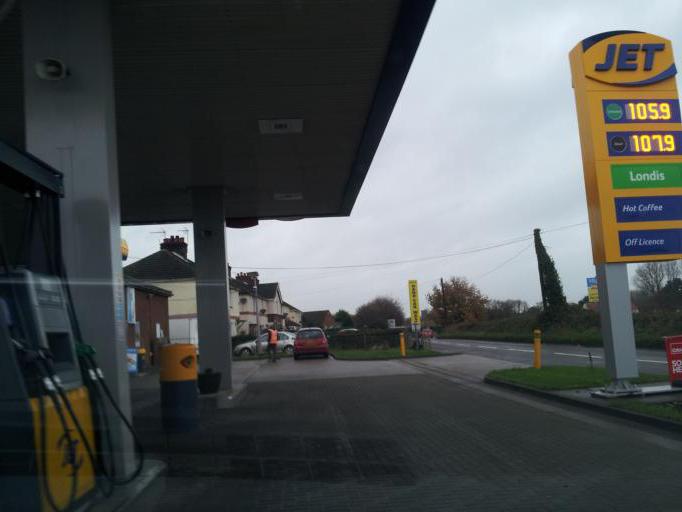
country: GB
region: England
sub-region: Norfolk
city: Hemsby
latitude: 52.6894
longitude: 1.6943
